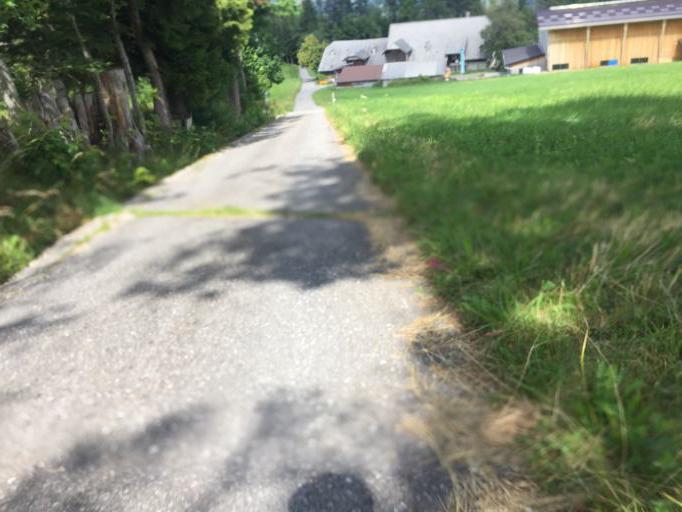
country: CH
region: Bern
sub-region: Thun District
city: Burgistein
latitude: 46.7576
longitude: 7.4483
